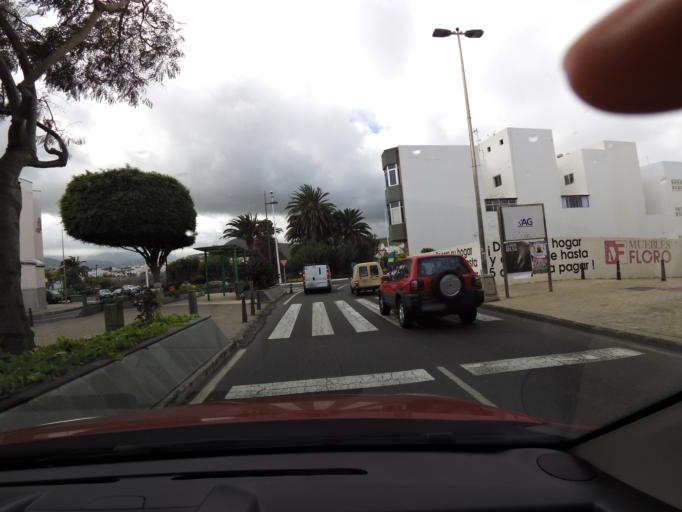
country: ES
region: Canary Islands
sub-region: Provincia de Las Palmas
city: Telde
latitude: 27.9993
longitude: -15.4192
